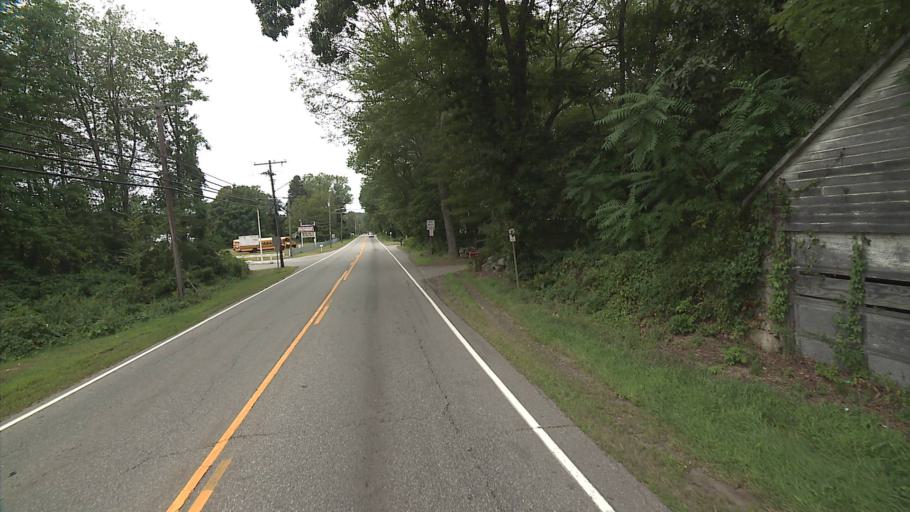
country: US
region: Connecticut
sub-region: New London County
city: Oxoboxo River
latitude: 41.3983
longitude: -72.1717
